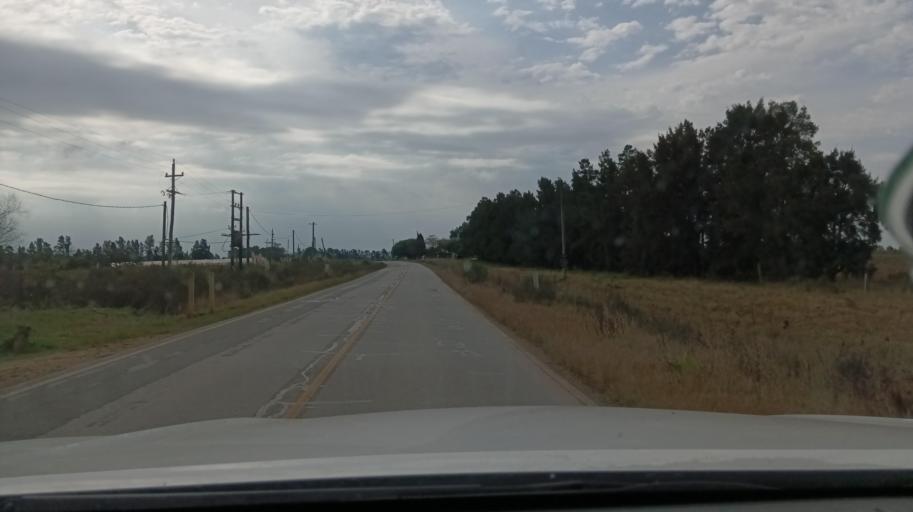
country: UY
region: Canelones
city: Sauce
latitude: -34.6459
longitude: -56.1064
